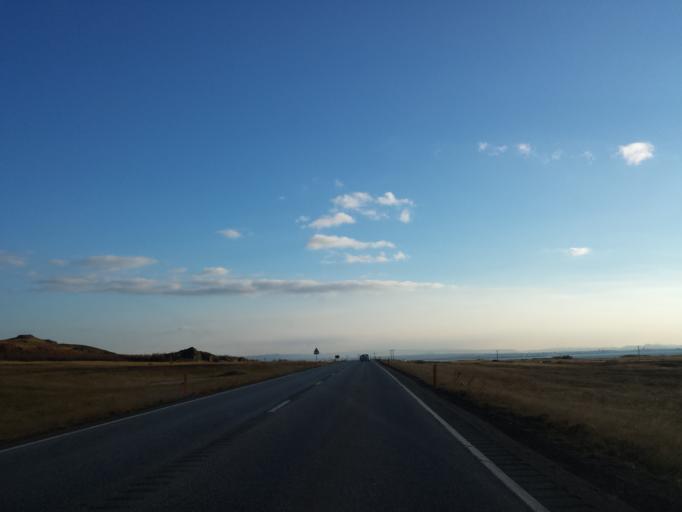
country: IS
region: Capital Region
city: Reykjavik
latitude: 64.2614
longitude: -21.8331
